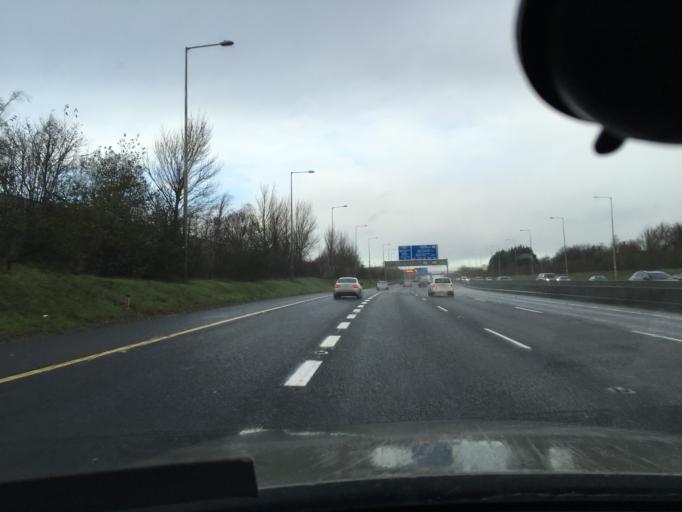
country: IE
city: Cherry Orchard
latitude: 53.3417
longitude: -6.3877
